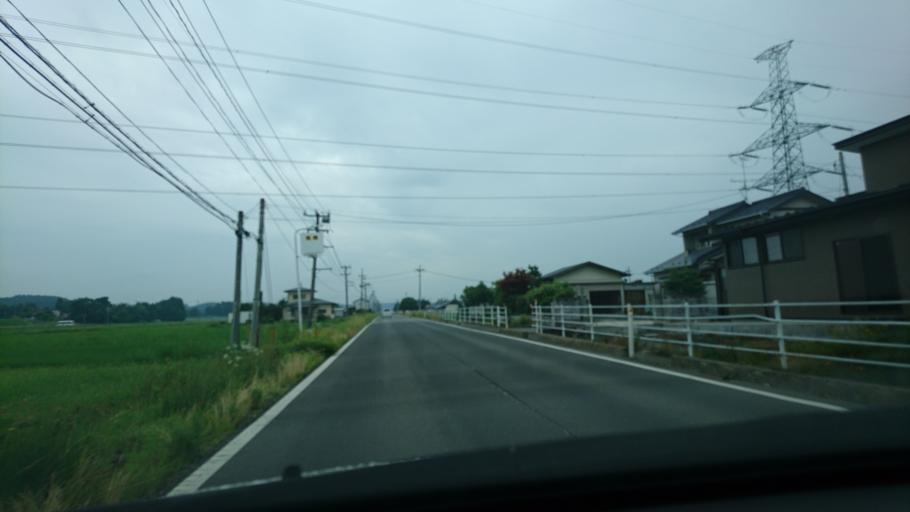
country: JP
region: Miyagi
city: Furukawa
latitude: 38.7314
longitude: 140.9748
